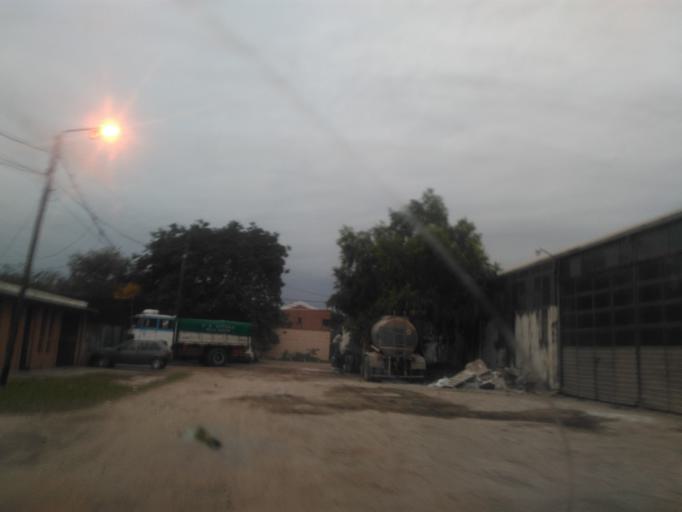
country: AR
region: Chaco
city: Fontana
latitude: -27.4421
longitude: -59.0214
